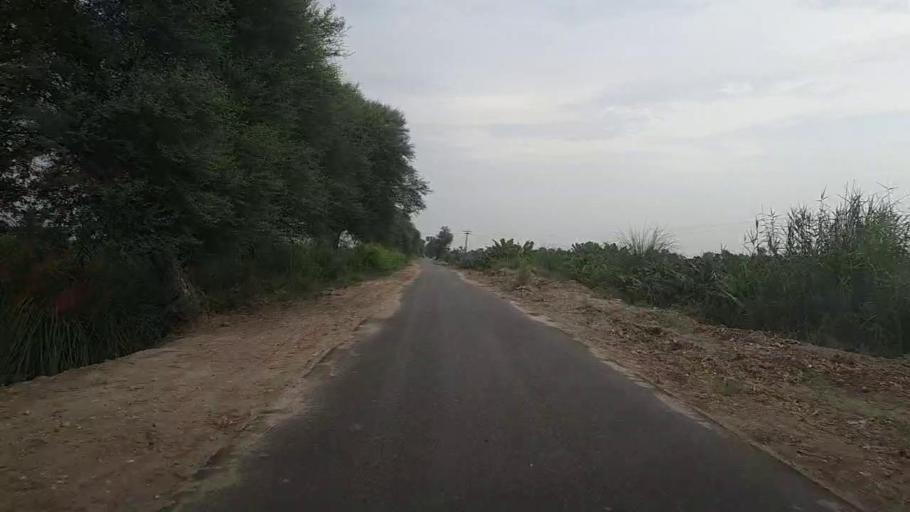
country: PK
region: Sindh
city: Karaundi
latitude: 26.9811
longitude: 68.3569
